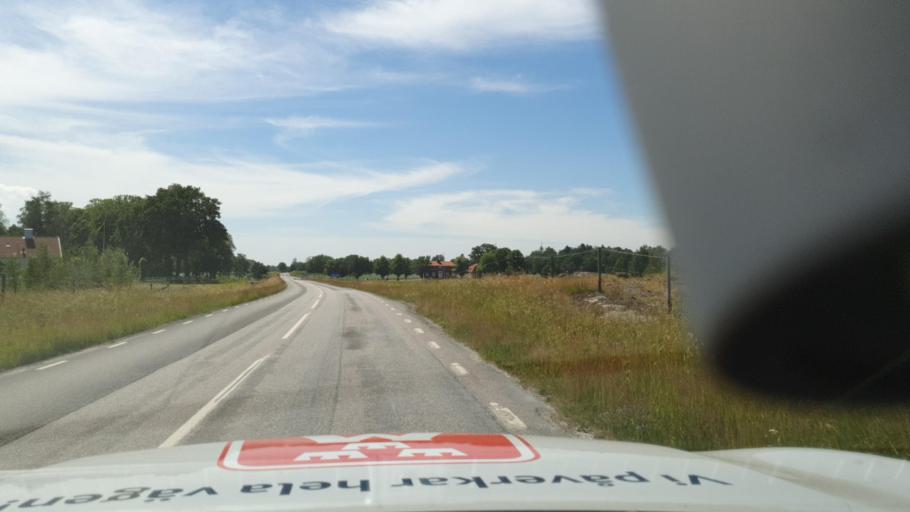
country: SE
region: Vaestra Goetaland
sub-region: Lidkopings Kommun
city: Lidkoping
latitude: 58.5093
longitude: 13.0115
